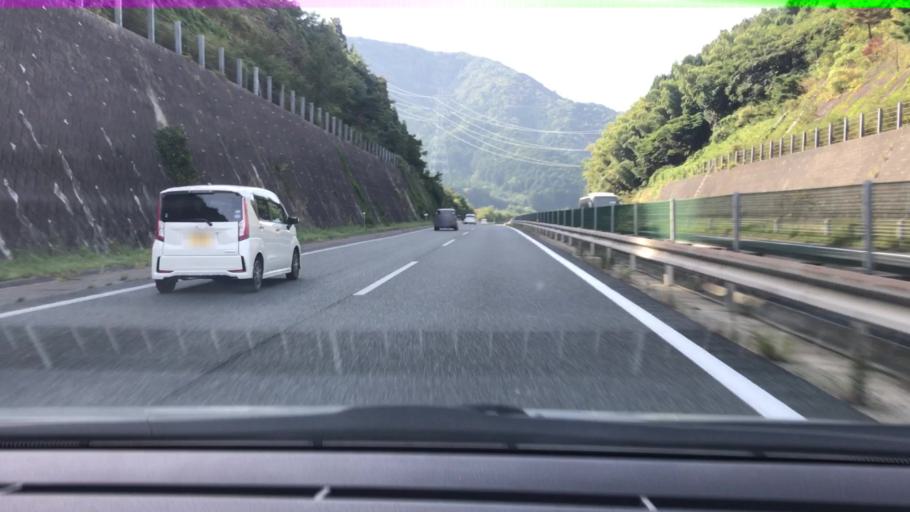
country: JP
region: Hyogo
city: Sasayama
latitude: 35.0411
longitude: 135.1826
